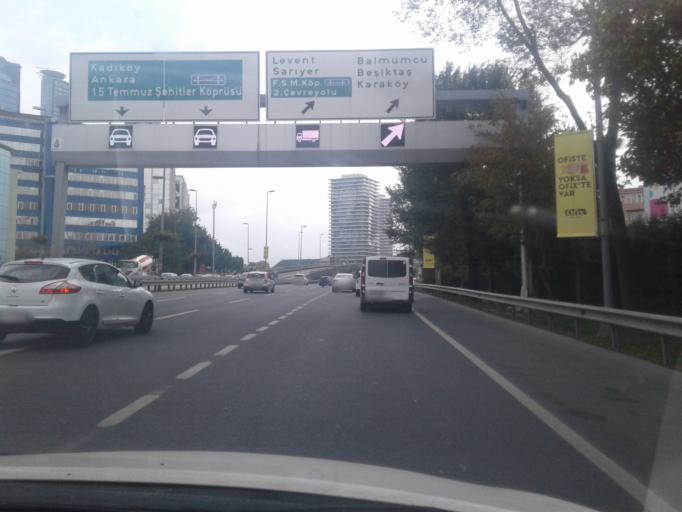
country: TR
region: Istanbul
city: Sisli
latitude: 41.0668
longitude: 29.0089
